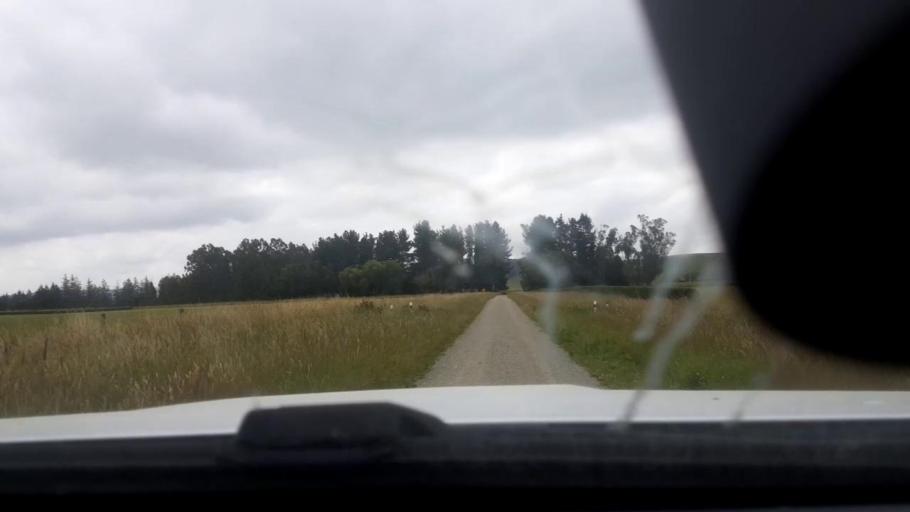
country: NZ
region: Canterbury
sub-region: Timaru District
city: Pleasant Point
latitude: -44.2228
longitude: 171.1634
